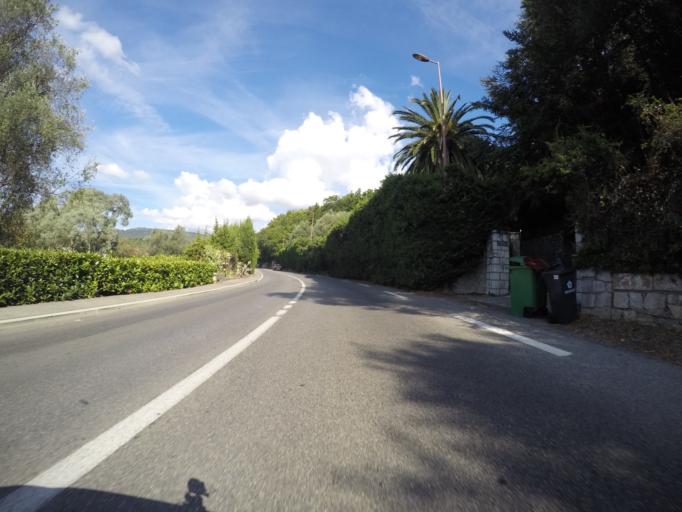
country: FR
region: Provence-Alpes-Cote d'Azur
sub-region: Departement des Alpes-Maritimes
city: Opio
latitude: 43.6761
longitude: 6.9840
